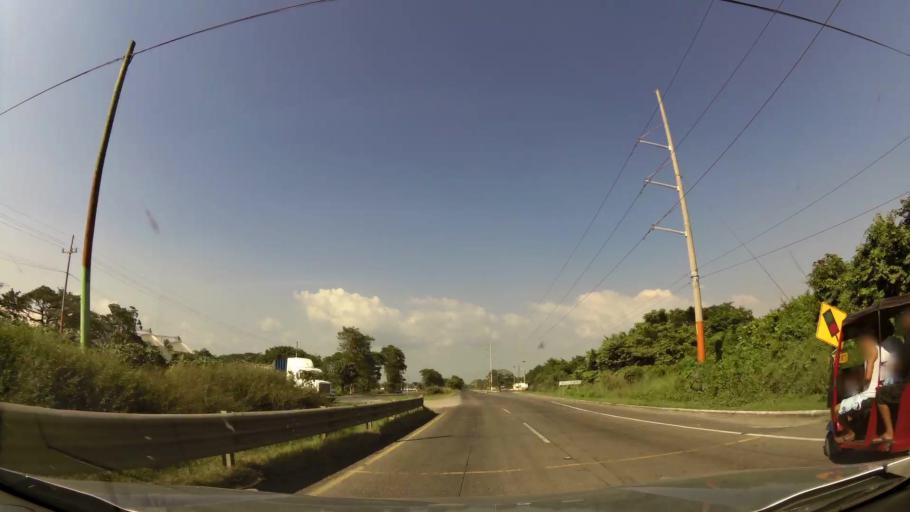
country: GT
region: Escuintla
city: Puerto San Jose
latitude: 13.9613
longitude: -90.7884
